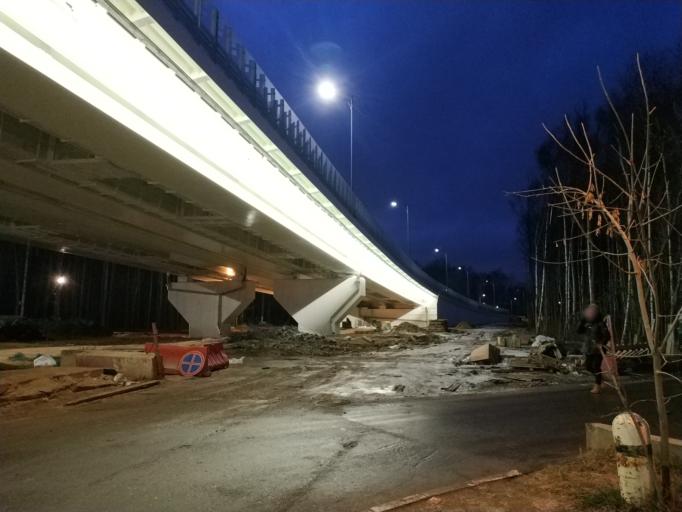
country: RU
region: Moskovskaya
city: Reutov
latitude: 55.7581
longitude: 37.8856
